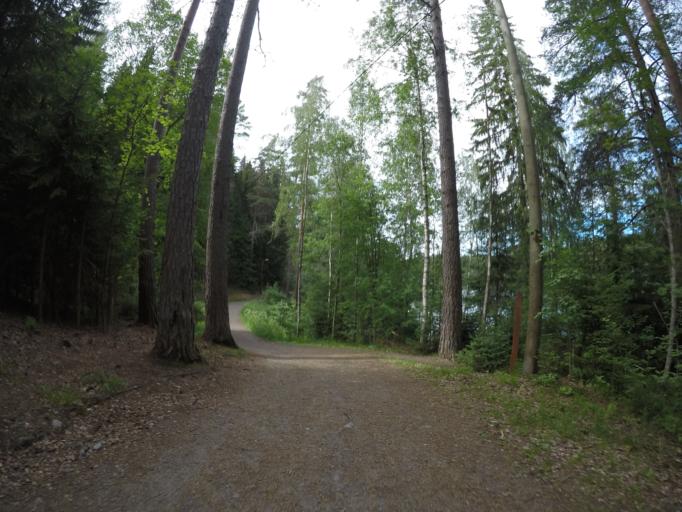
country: FI
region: Haeme
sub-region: Haemeenlinna
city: Haemeenlinna
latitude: 60.9936
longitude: 24.4176
